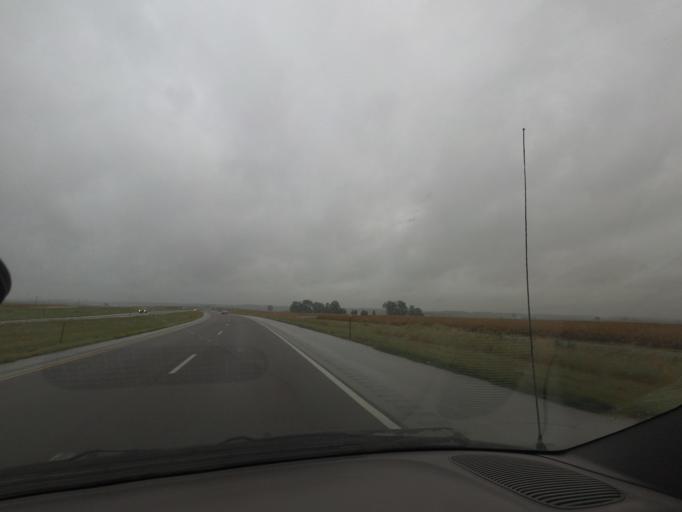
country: US
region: Missouri
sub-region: Marion County
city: Hannibal
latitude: 39.7401
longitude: -91.3041
